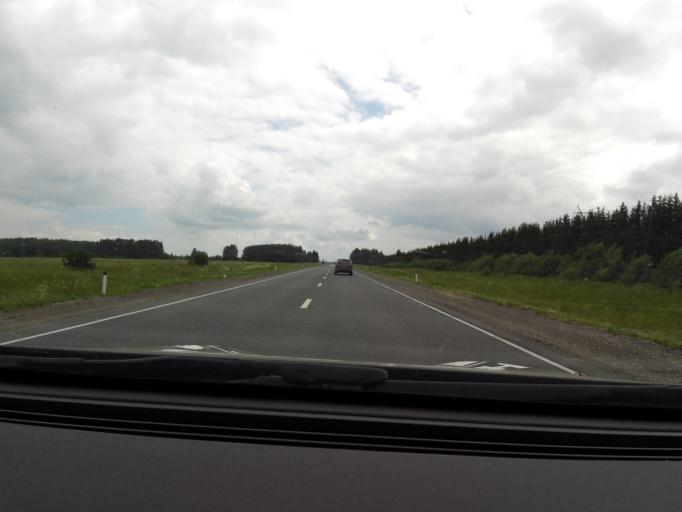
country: RU
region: Perm
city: Orda
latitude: 57.2721
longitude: 57.0112
